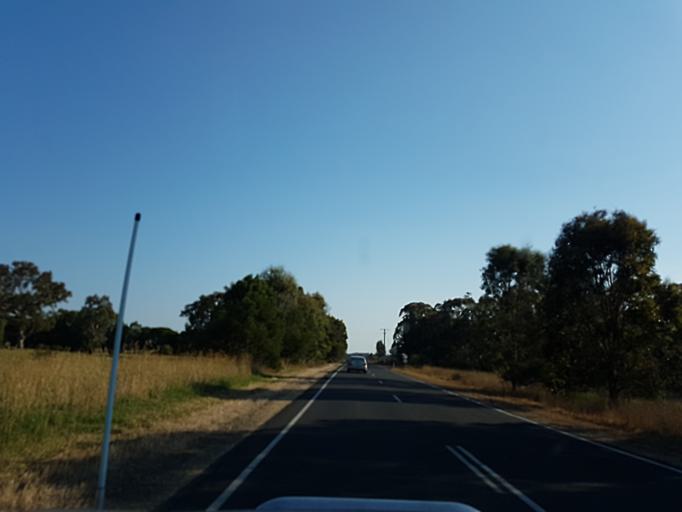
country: AU
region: Victoria
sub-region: Wellington
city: Sale
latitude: -38.0740
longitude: 147.0213
